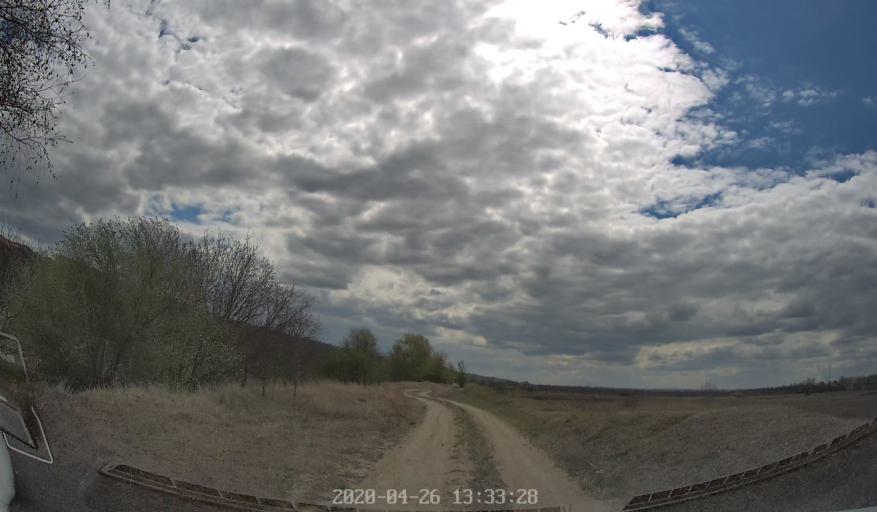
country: MD
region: Criuleni
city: Criuleni
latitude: 47.2079
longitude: 29.1777
